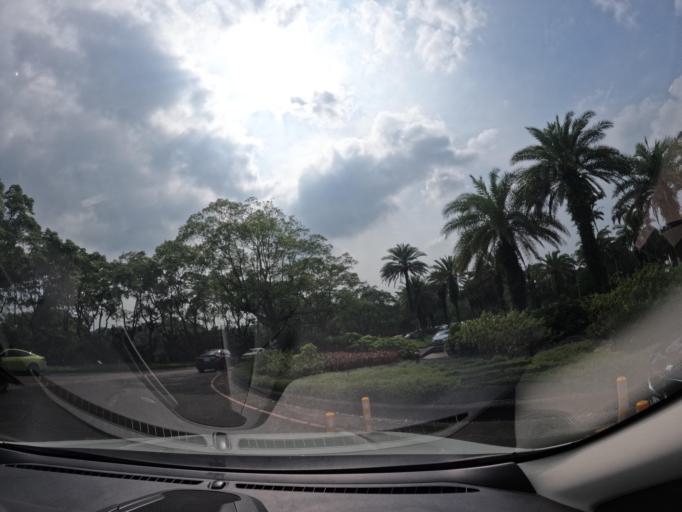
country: TW
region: Taiwan
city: Daxi
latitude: 24.8807
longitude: 121.3266
